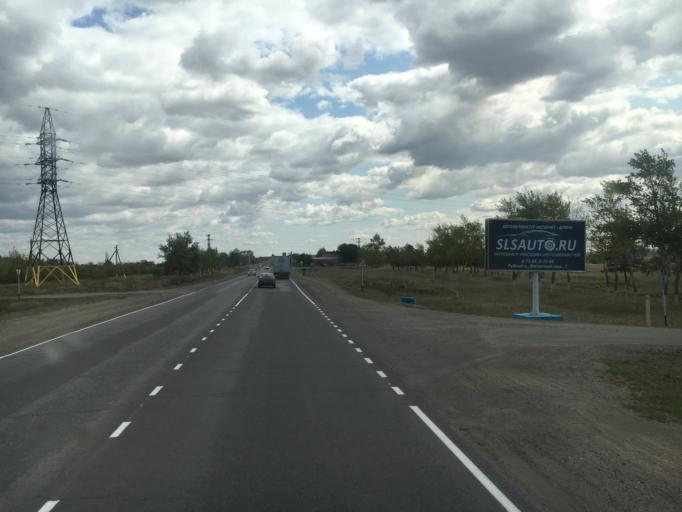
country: KZ
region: Qostanay
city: Rudnyy
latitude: 52.9658
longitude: 63.1654
